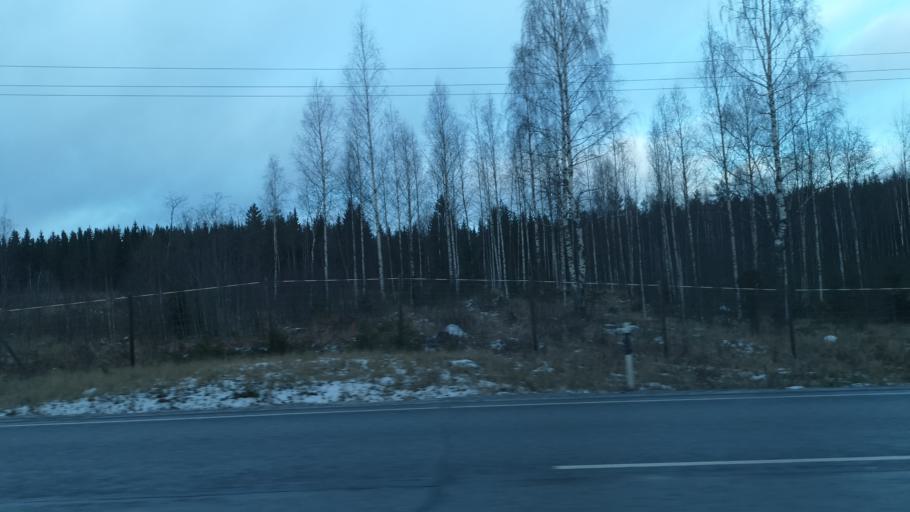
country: FI
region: Southern Savonia
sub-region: Mikkeli
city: Pertunmaa
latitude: 61.4358
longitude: 26.5408
